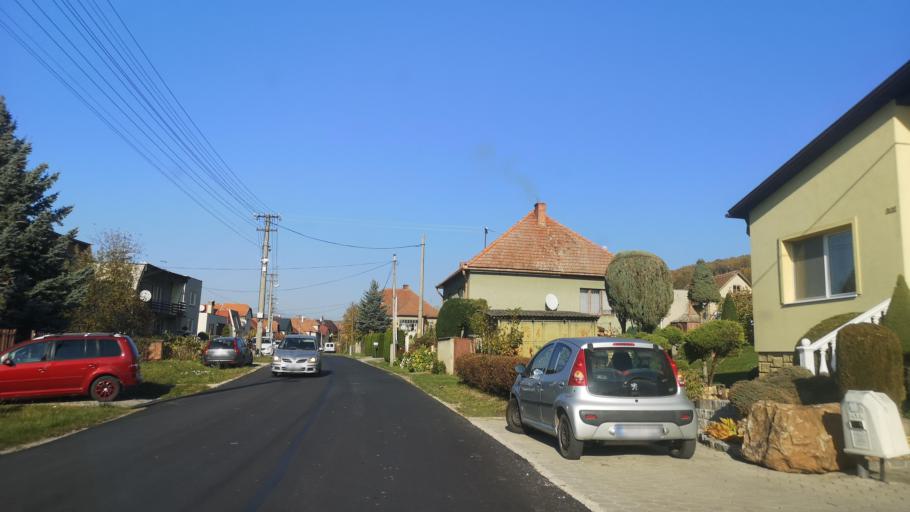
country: SK
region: Nitriansky
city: Zlate Moravce
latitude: 48.4450
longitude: 18.4346
